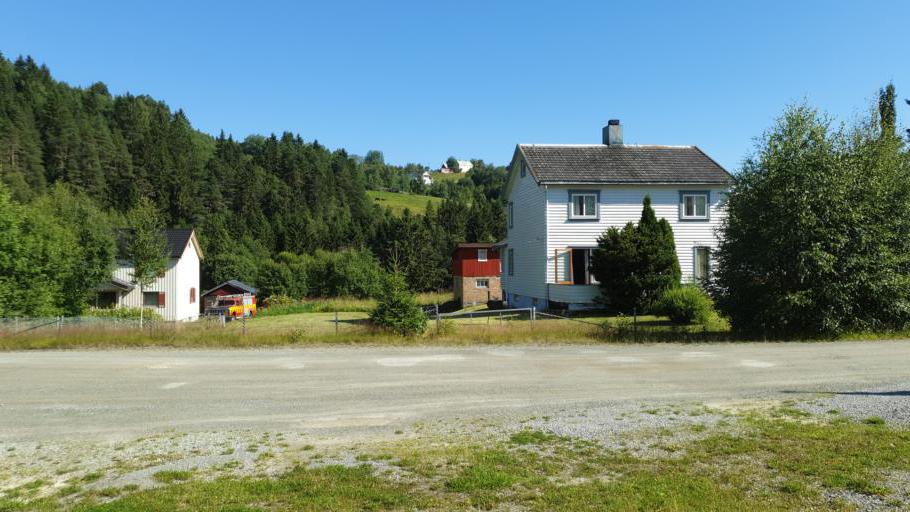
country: NO
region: Sor-Trondelag
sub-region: Meldal
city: Meldal
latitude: 63.1692
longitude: 9.7480
